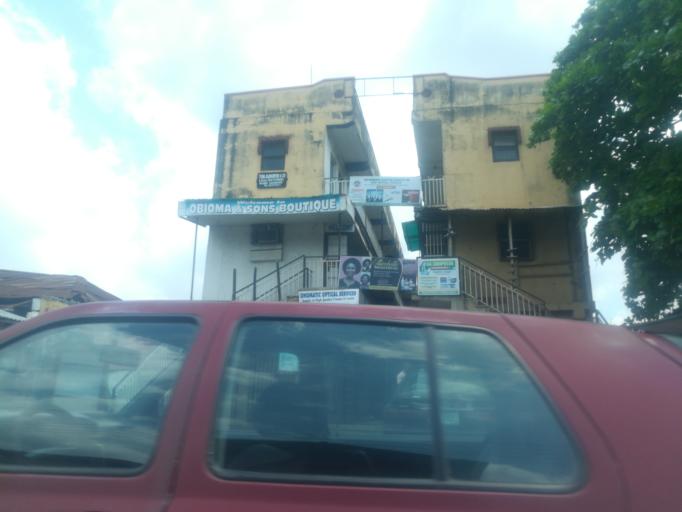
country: NG
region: Oyo
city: Ibadan
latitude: 7.3916
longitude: 3.8830
